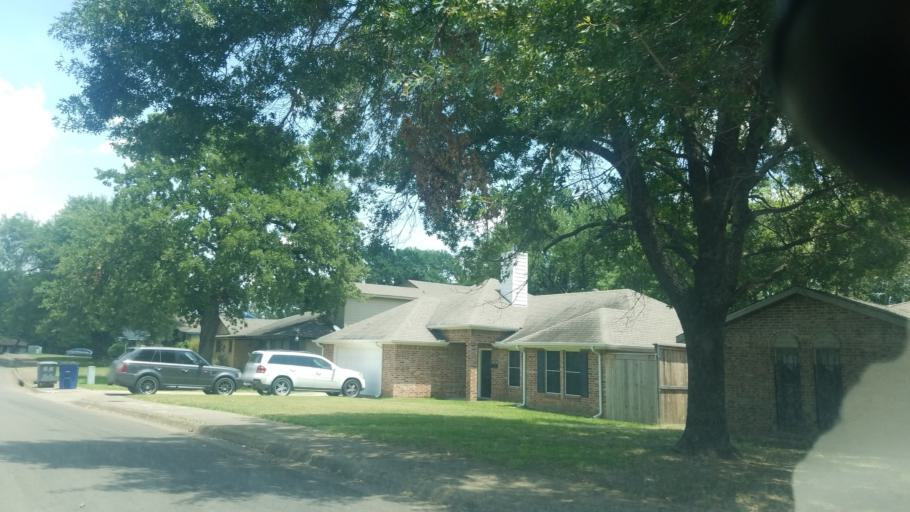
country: US
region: Texas
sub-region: Dallas County
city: Dallas
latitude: 32.7198
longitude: -96.7773
